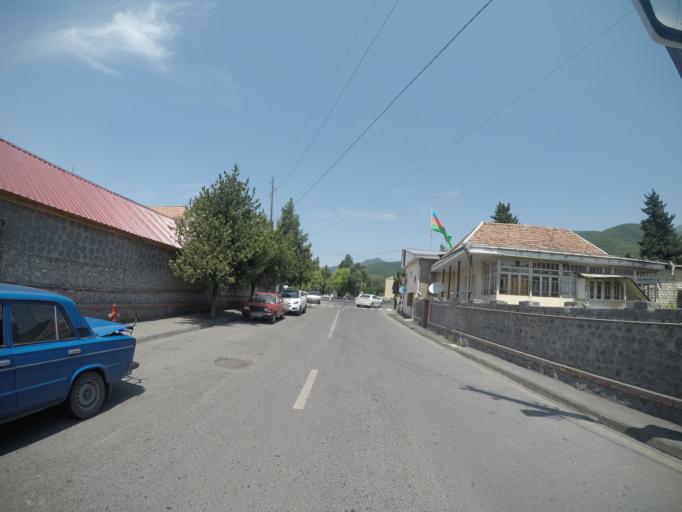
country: AZ
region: Qakh Rayon
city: Qax
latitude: 41.4190
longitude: 46.9185
